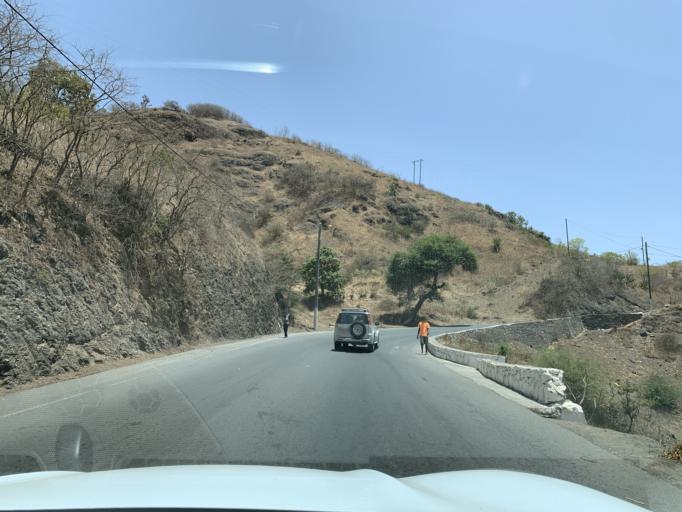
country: CV
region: Sao Domingos
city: Sao Domingos
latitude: 15.0431
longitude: -23.5760
